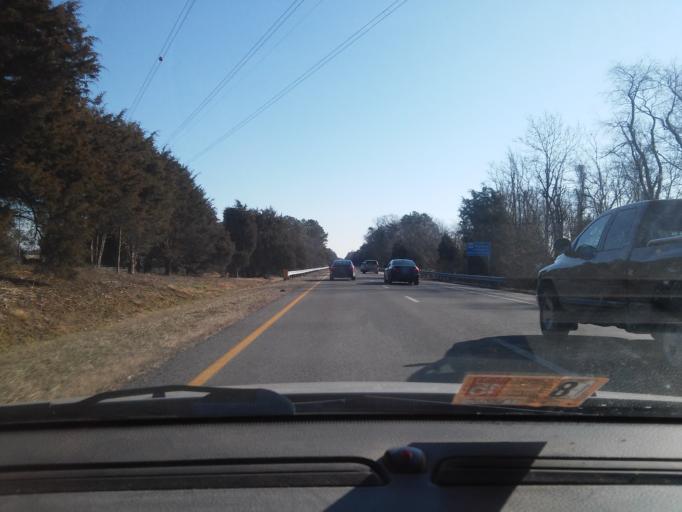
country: US
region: Virginia
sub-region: Henrico County
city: Wyndham
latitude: 37.6992
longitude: -77.7409
